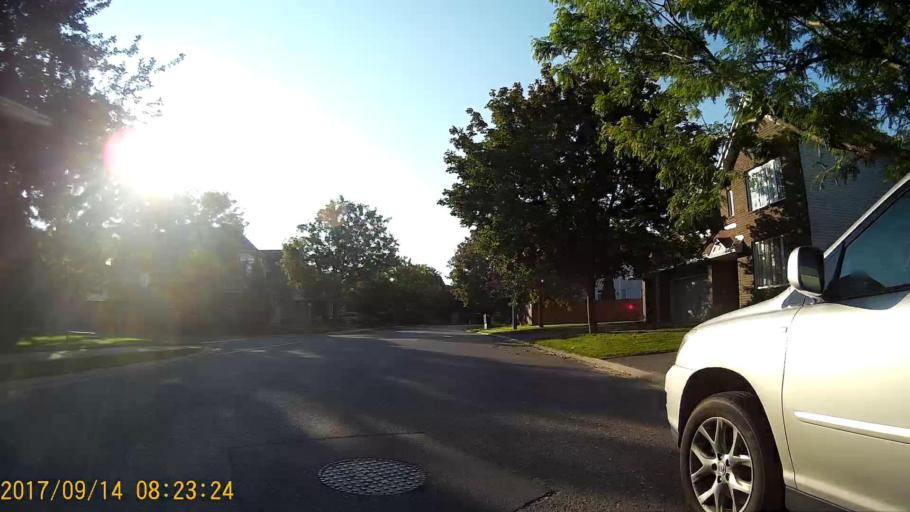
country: CA
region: Ontario
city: Bells Corners
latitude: 45.3512
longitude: -75.9306
